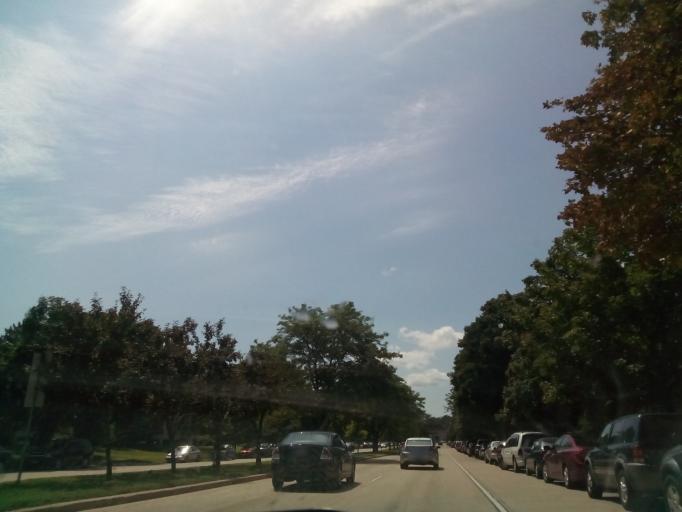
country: US
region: Wisconsin
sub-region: Dane County
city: Madison
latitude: 43.0662
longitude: -89.3964
